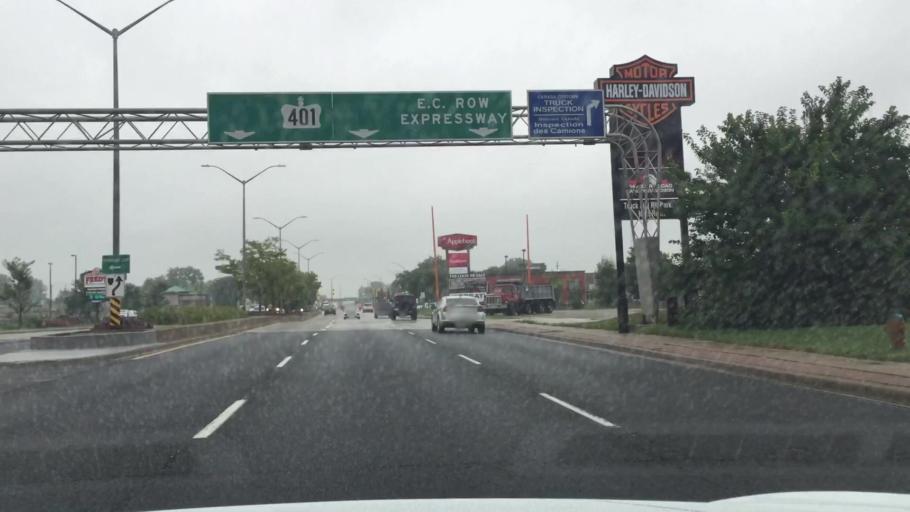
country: CA
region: Ontario
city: Windsor
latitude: 42.2776
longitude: -83.0521
